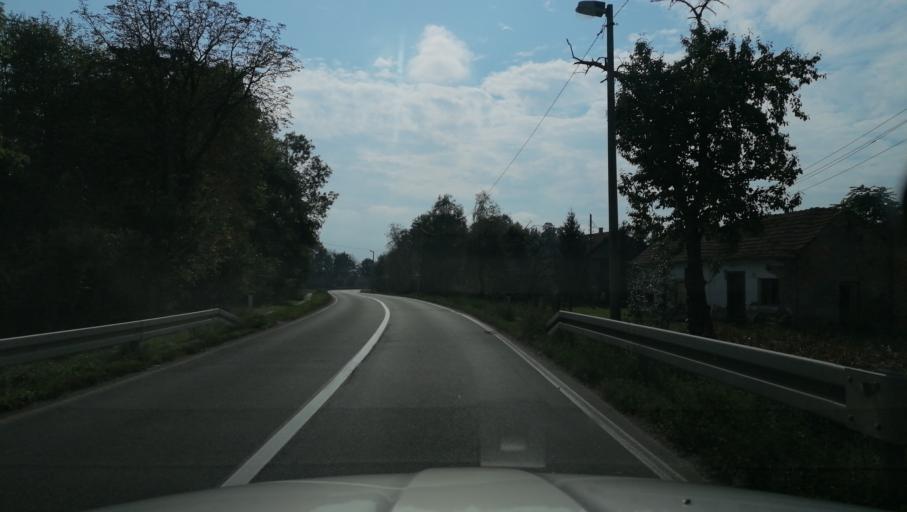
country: BA
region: Republika Srpska
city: Balatun
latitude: 44.8602
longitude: 19.3240
